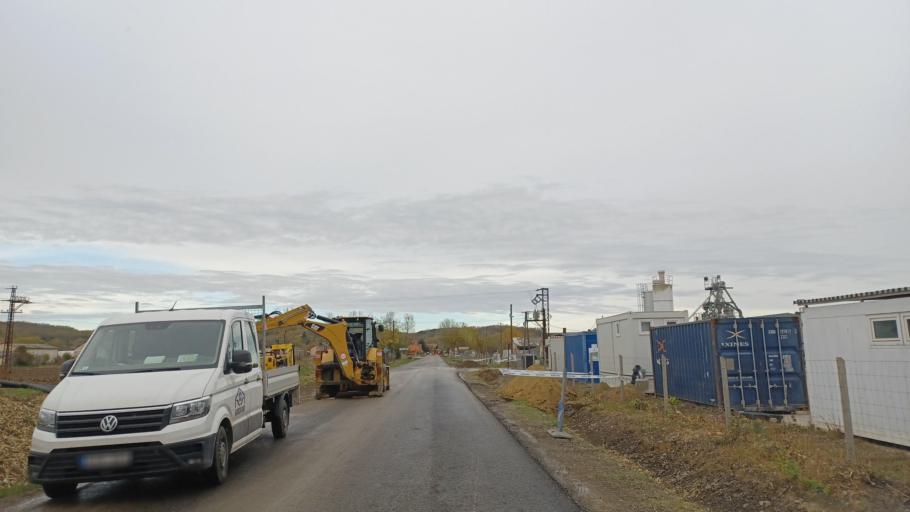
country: HU
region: Tolna
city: Dunaszentgyorgy
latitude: 46.5234
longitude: 18.7724
